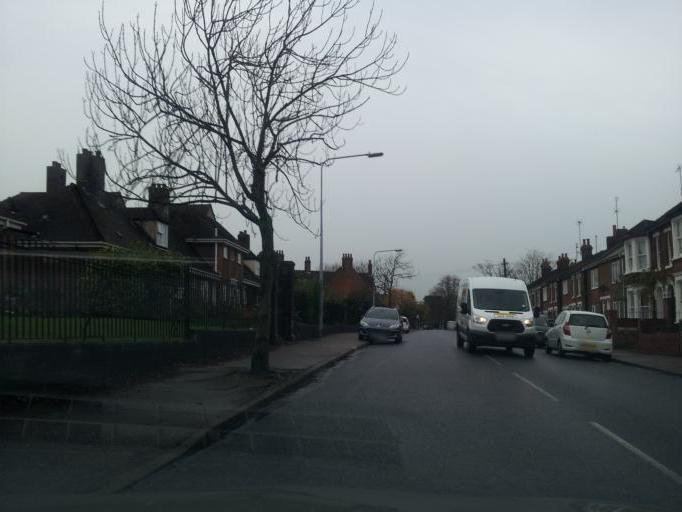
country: GB
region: England
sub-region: Essex
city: Colchester
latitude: 51.8783
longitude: 0.9179
